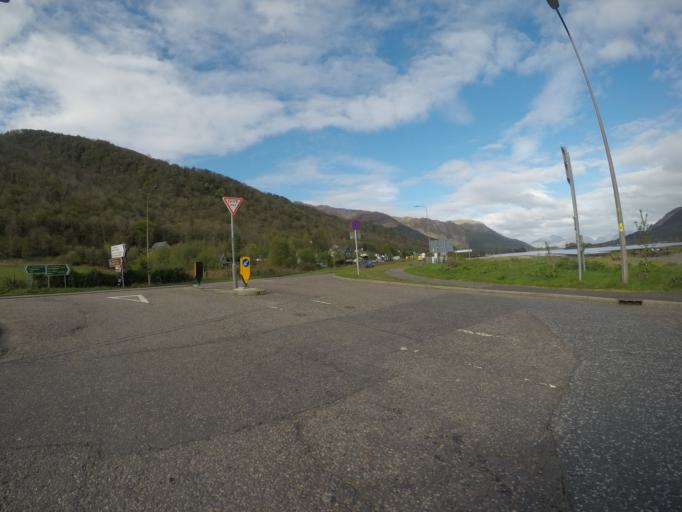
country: GB
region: Scotland
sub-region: Highland
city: Fort William
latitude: 56.6816
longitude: -5.1073
